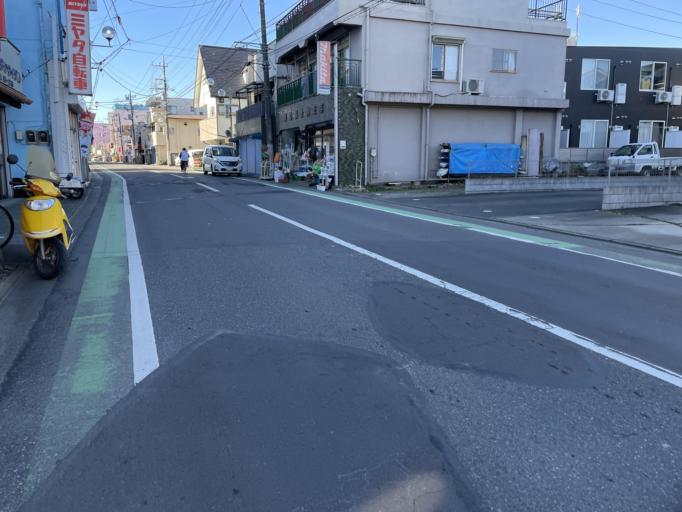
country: JP
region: Saitama
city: Sakado
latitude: 35.9394
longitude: 139.4251
